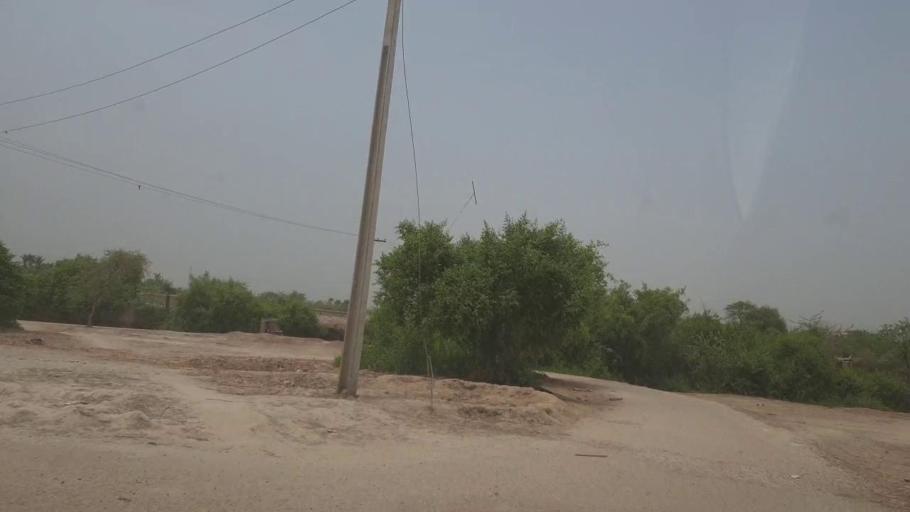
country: PK
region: Sindh
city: Kot Diji
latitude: 27.4409
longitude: 68.6435
